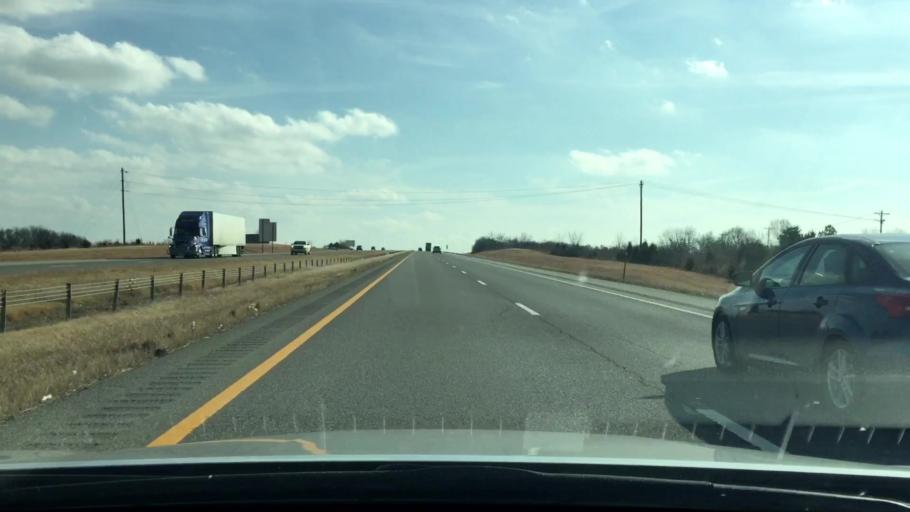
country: US
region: Oklahoma
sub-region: McClain County
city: Purcell
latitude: 34.9675
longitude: -97.3704
